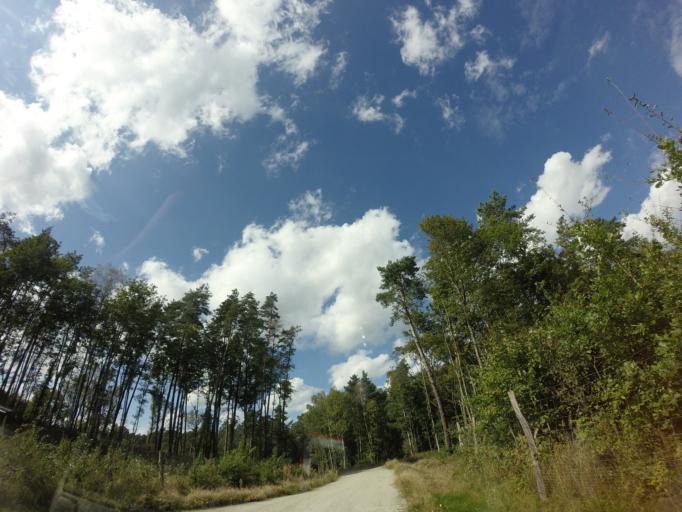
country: PL
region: West Pomeranian Voivodeship
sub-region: Powiat choszczenski
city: Recz
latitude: 53.2983
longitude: 15.5988
